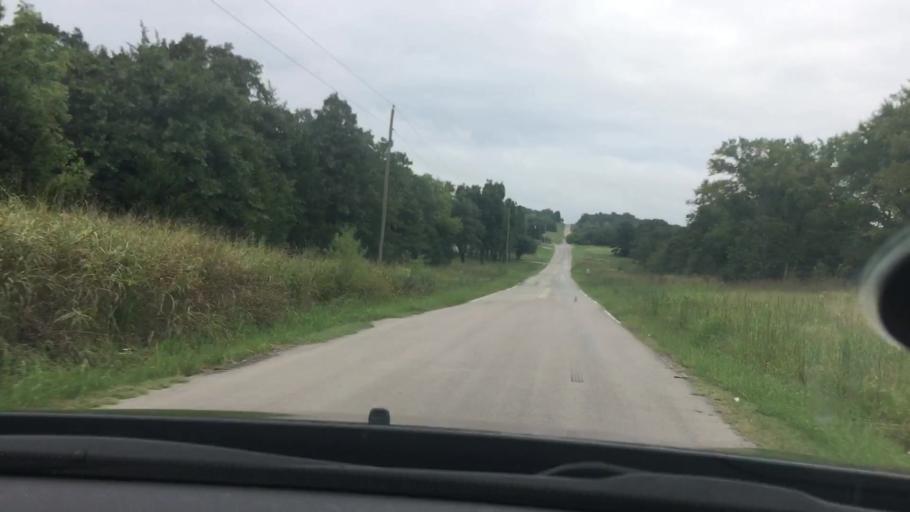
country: US
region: Oklahoma
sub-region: Pontotoc County
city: Ada
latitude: 34.7989
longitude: -96.5474
